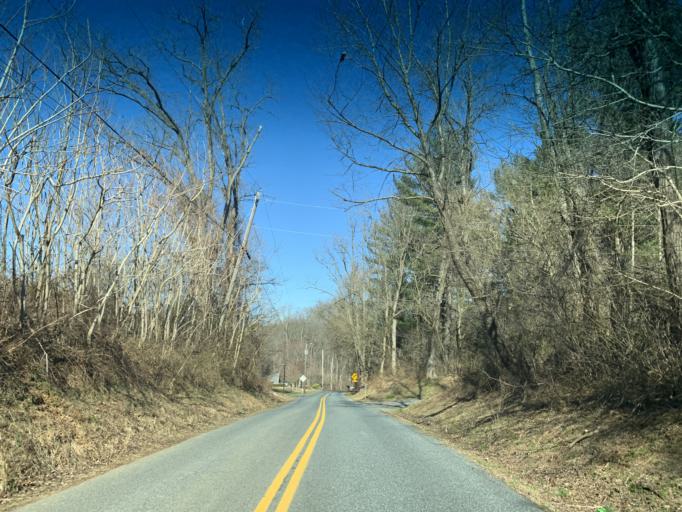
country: US
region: Maryland
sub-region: Harford County
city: Aberdeen
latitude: 39.6296
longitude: -76.2299
